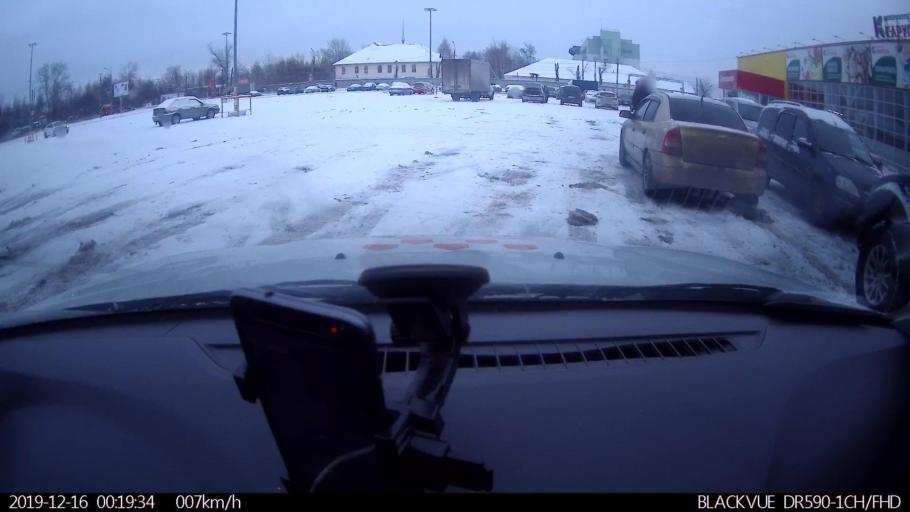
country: RU
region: Nizjnij Novgorod
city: Gorbatovka
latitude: 56.3114
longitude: 43.8389
